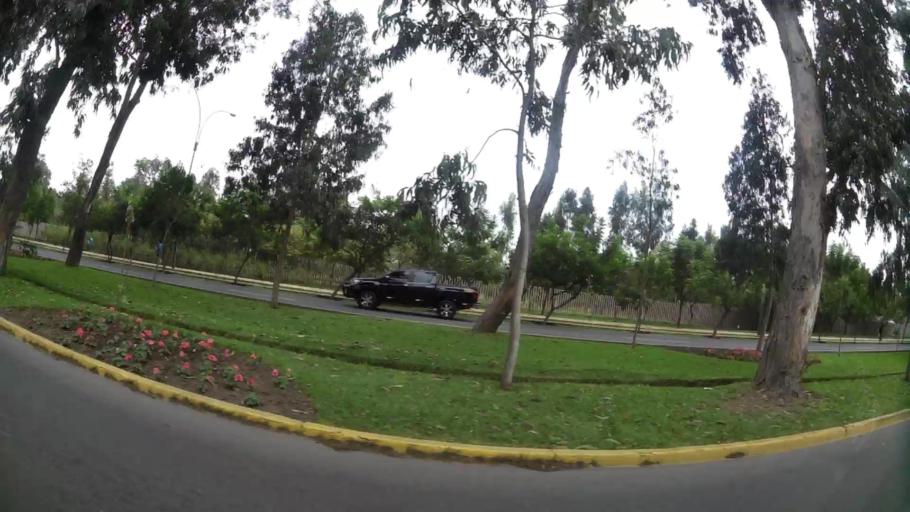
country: PE
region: Lima
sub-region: Lima
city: San Luis
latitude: -12.1057
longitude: -76.9848
